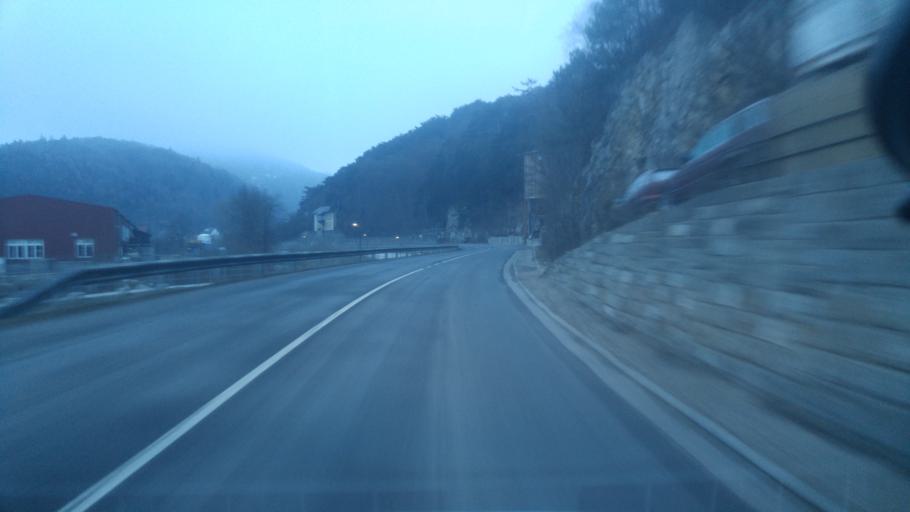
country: AT
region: Lower Austria
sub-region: Politischer Bezirk Baden
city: Weissenbach an der Triesting
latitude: 47.9843
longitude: 16.0420
